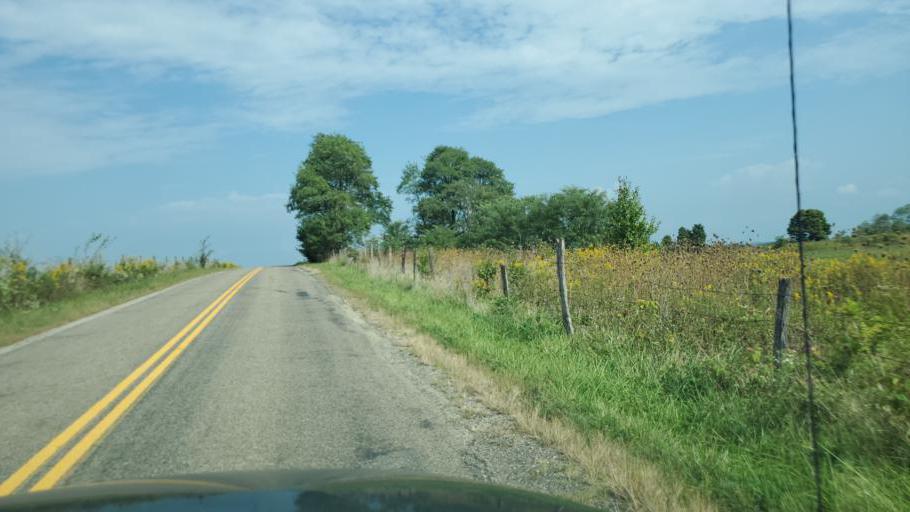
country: US
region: Ohio
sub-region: Muskingum County
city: Zanesville
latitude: 39.9392
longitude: -82.0854
